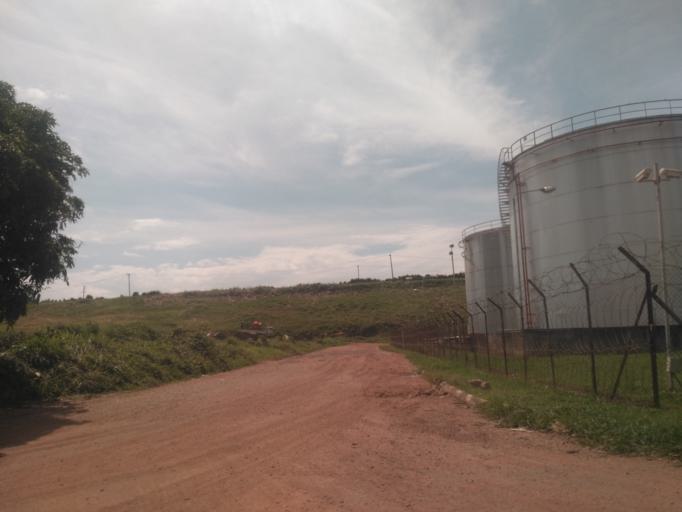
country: UG
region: Central Region
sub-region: Wakiso District
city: Entebbe
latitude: 0.0434
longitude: 32.4451
